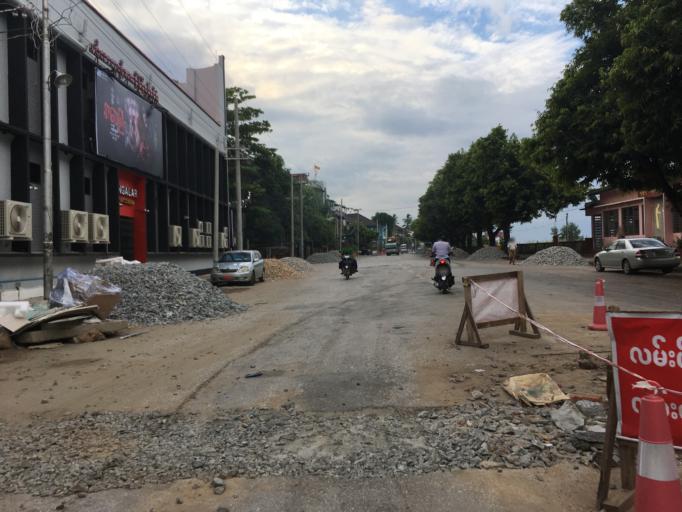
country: MM
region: Mon
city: Mawlamyine
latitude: 16.4886
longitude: 97.6181
